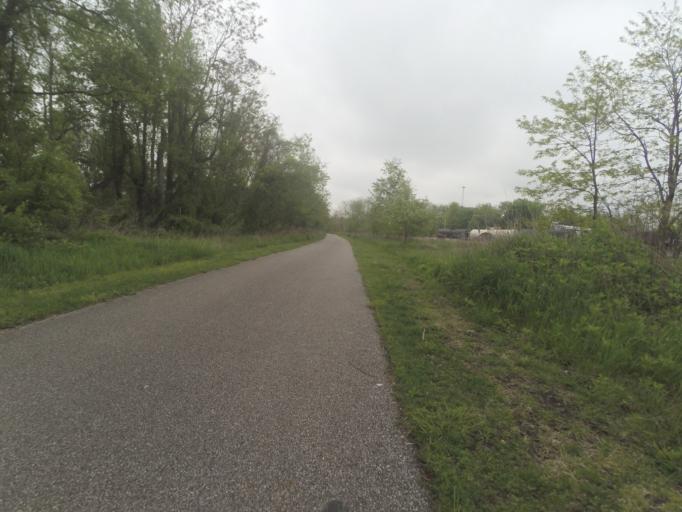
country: US
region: Ohio
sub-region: Portage County
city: Kent
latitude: 41.1658
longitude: -81.3432
